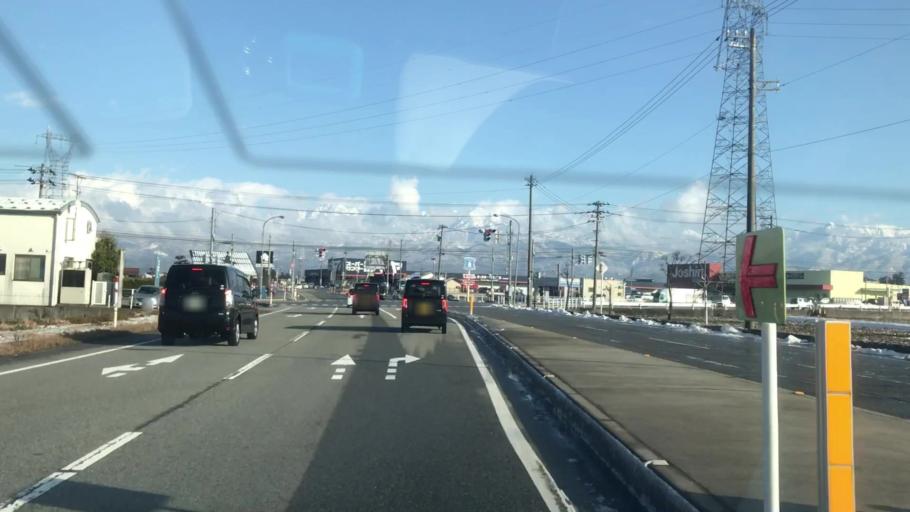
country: JP
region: Toyama
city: Kamiichi
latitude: 36.6866
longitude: 137.2909
